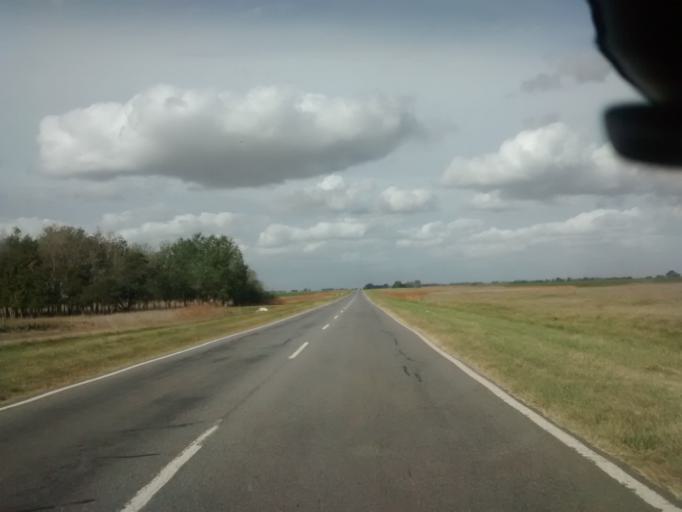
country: AR
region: Buenos Aires
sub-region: Partido de Balcarce
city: Balcarce
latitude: -37.6694
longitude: -58.5299
